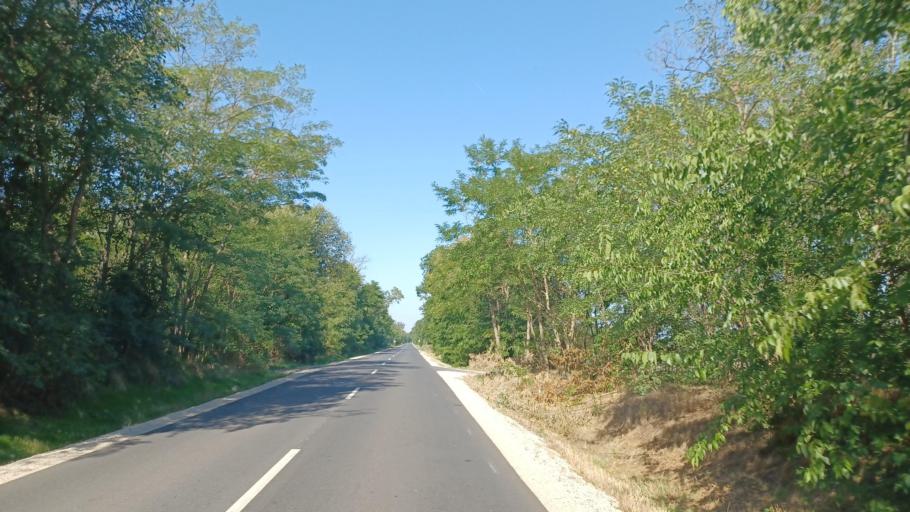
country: HU
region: Tolna
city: Nemetker
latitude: 46.7348
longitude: 18.7189
